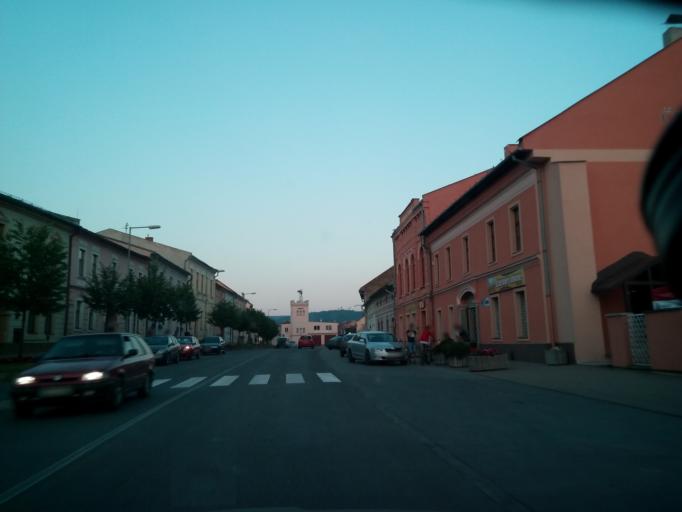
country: SK
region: Presovsky
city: Lubica
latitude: 49.1214
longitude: 20.4468
